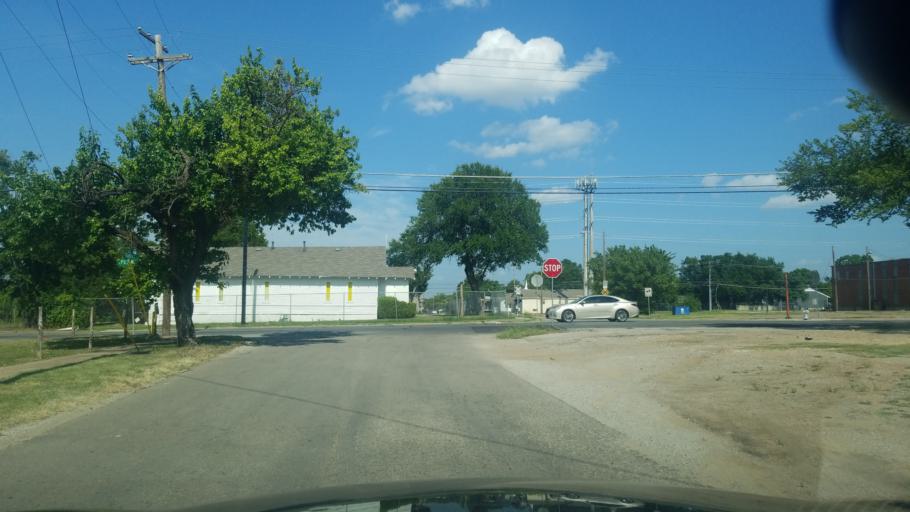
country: US
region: Texas
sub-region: Dallas County
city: Dallas
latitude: 32.7277
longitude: -96.8059
